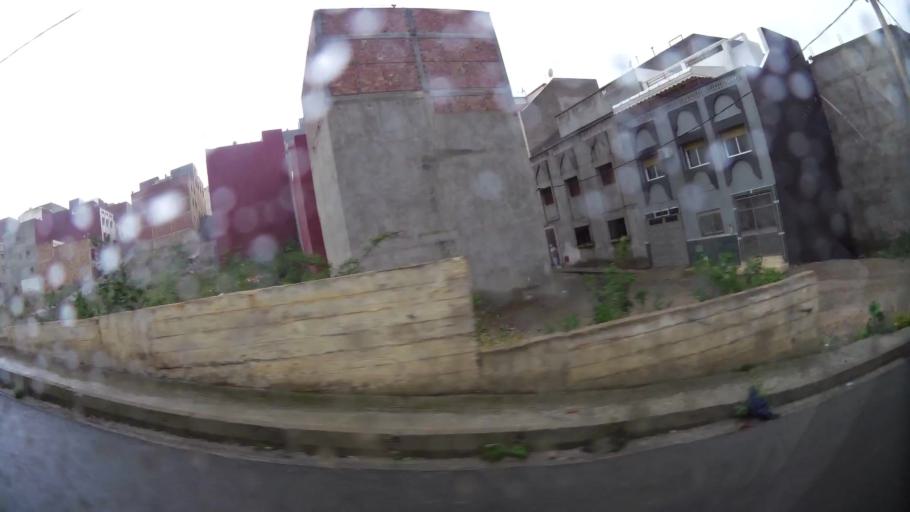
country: MA
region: Taza-Al Hoceima-Taounate
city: Al Hoceima
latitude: 35.2558
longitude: -3.9323
